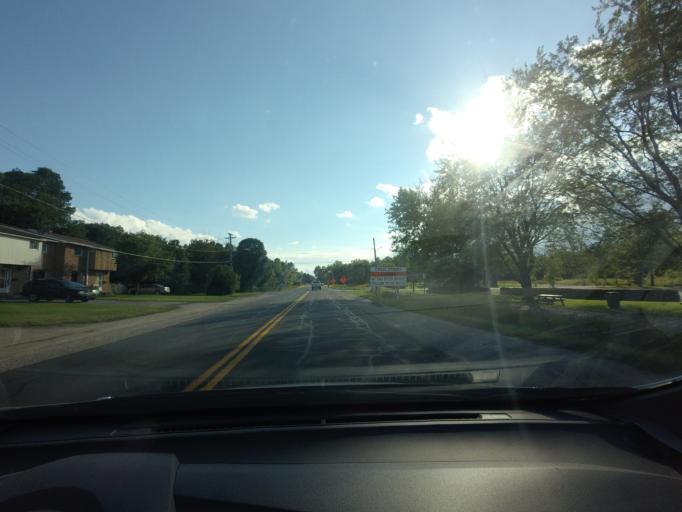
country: CA
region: Ontario
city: Perth
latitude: 44.9016
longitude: -76.2386
